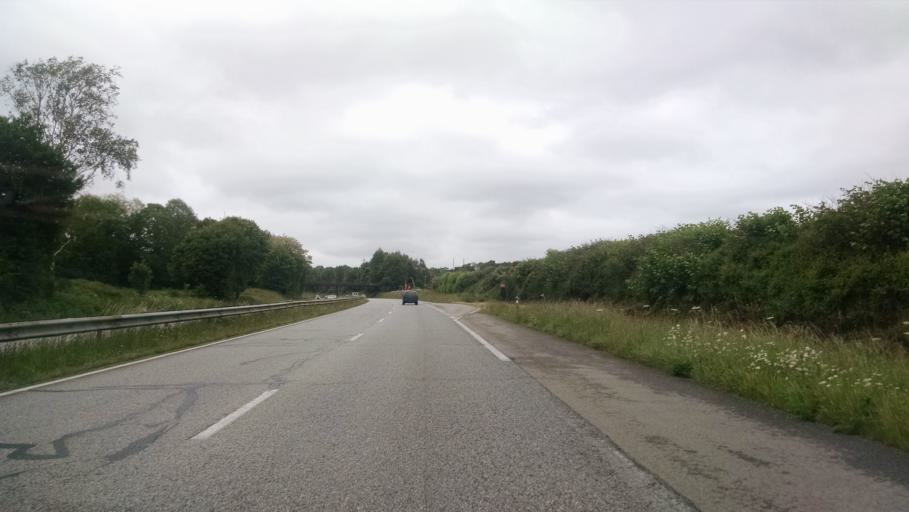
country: FR
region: Brittany
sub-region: Departement du Finistere
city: Quimper
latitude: 48.0058
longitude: -4.0623
